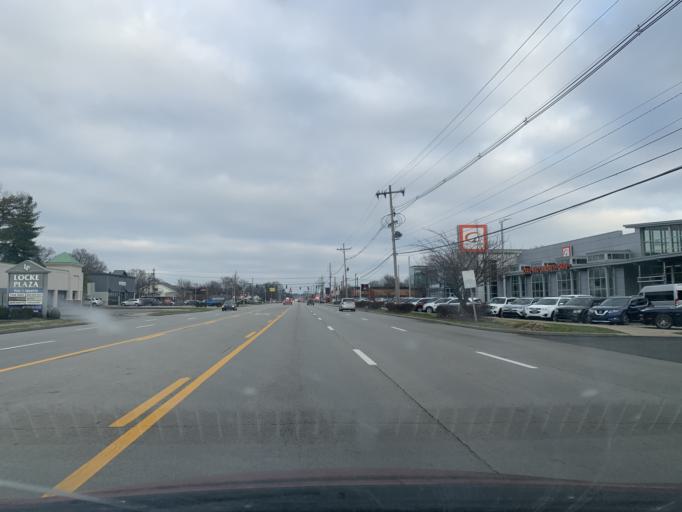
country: US
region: Kentucky
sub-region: Jefferson County
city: Beechwood Village
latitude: 38.2518
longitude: -85.6420
